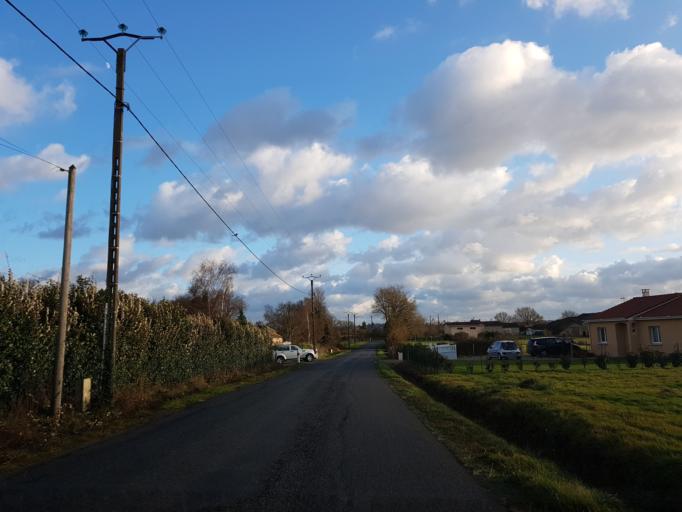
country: FR
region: Limousin
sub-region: Departement de la Haute-Vienne
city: Saint-Junien
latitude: 45.9290
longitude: 0.9284
